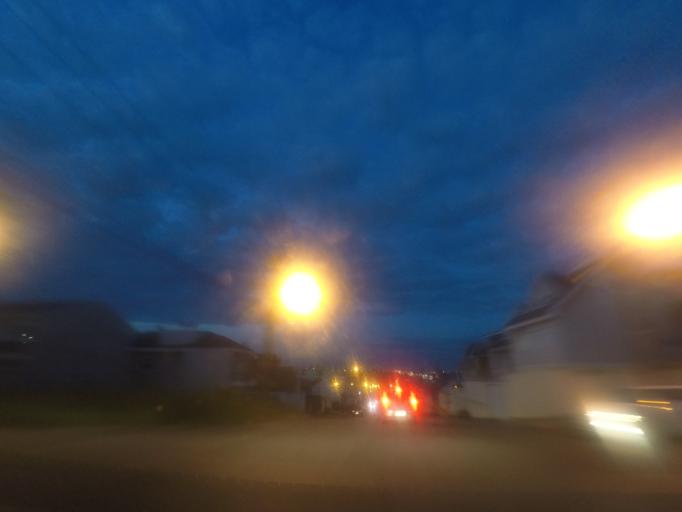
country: BR
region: Parana
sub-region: Pinhais
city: Pinhais
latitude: -25.3870
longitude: -49.2084
